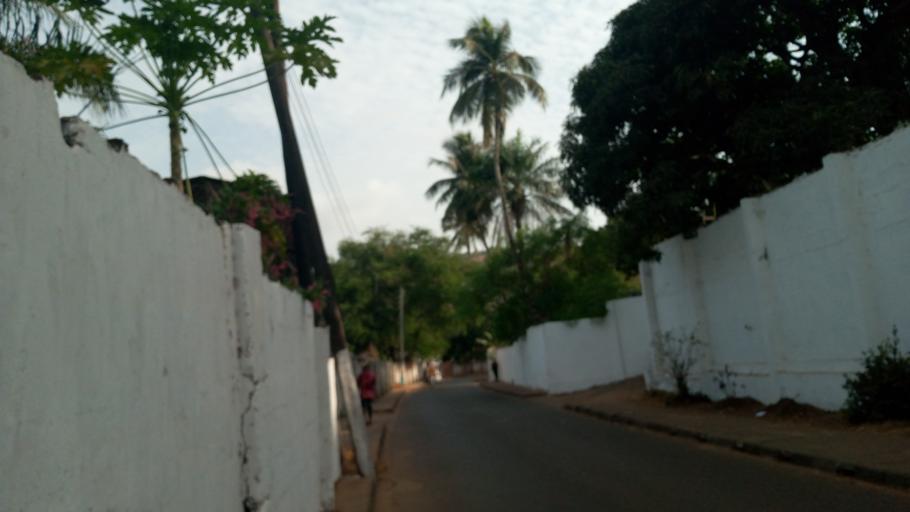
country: SL
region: Western Area
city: Freetown
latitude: 8.4787
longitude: -13.2578
